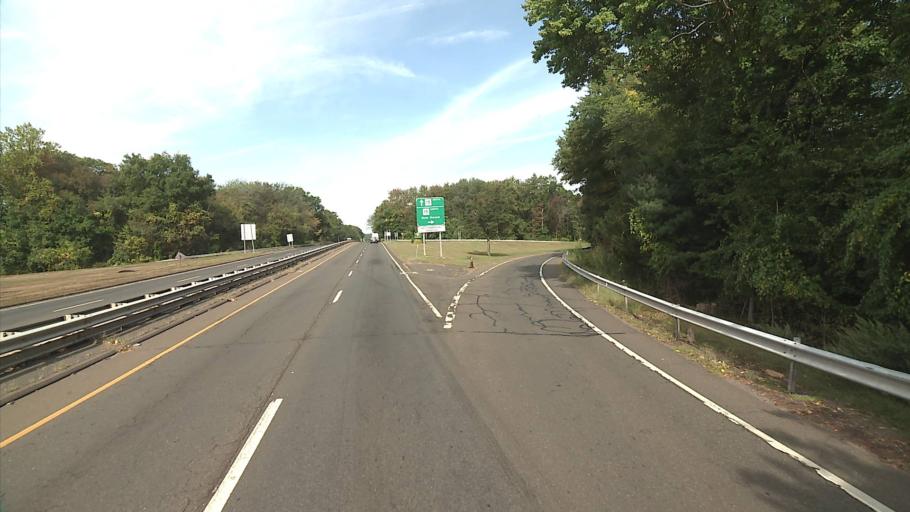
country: US
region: Connecticut
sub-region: New Haven County
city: Orange
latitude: 41.3051
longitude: -73.0320
